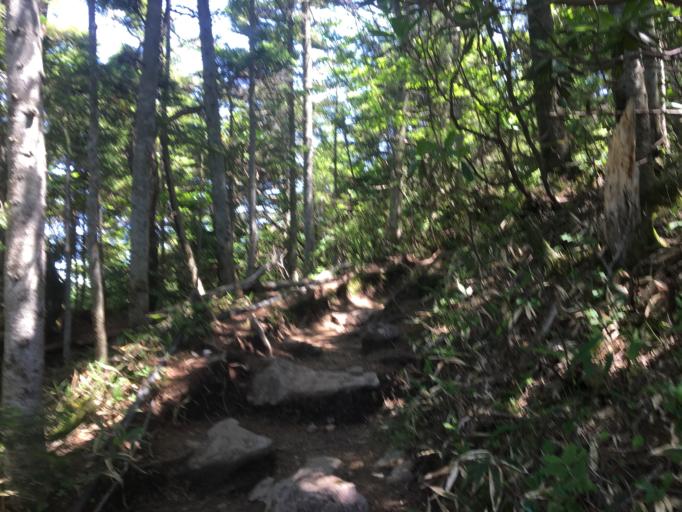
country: JP
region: Nagano
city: Komoro
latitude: 36.4019
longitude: 138.4825
